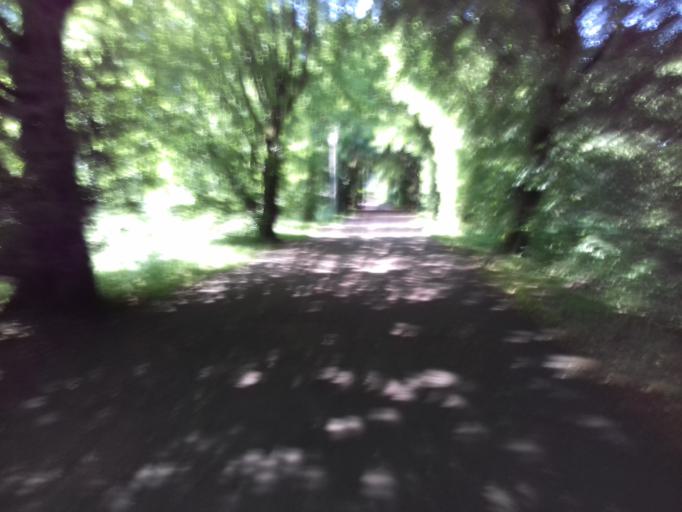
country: DE
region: Schleswig-Holstein
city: Neumunster
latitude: 54.0794
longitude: 10.0068
